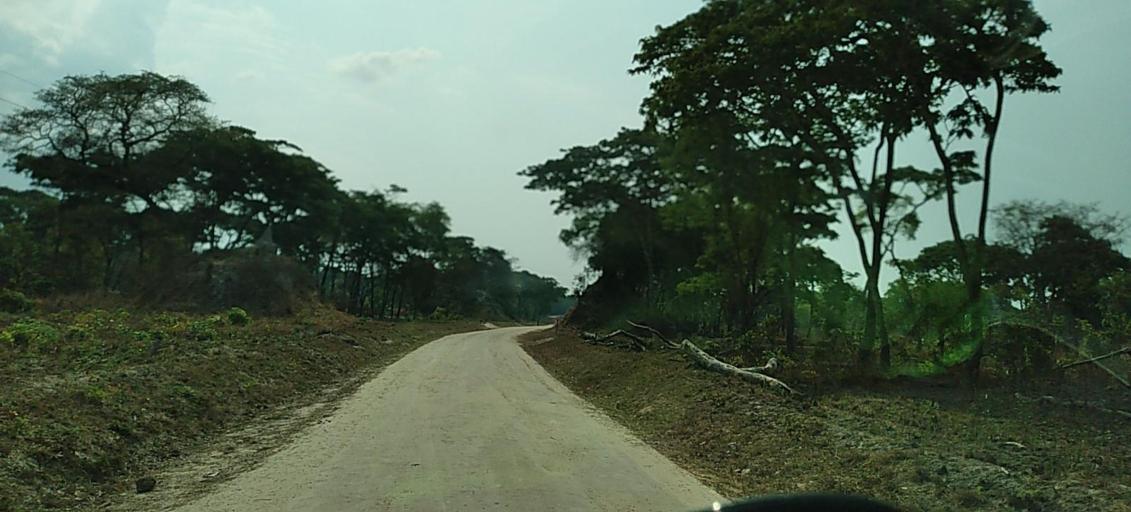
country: ZM
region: North-Western
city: Solwezi
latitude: -12.6968
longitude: 26.4087
